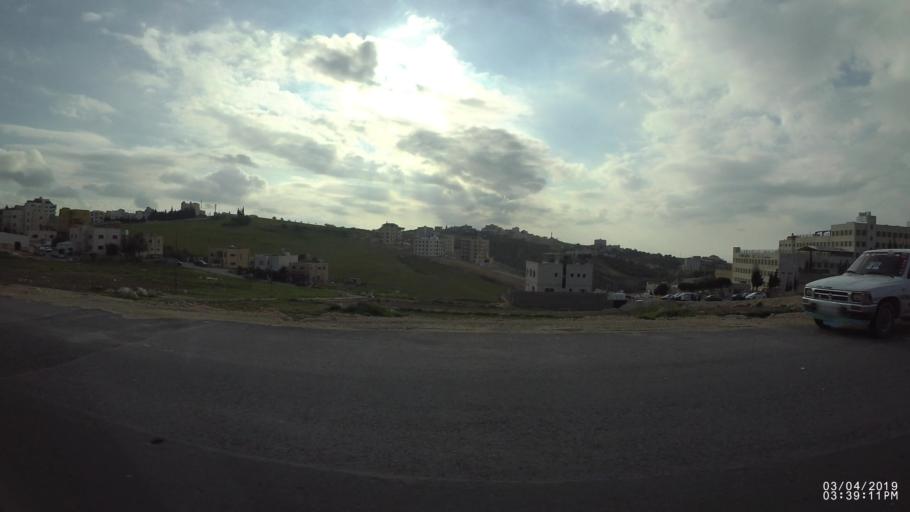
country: JO
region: Amman
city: Umm as Summaq
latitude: 31.9158
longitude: 35.8497
